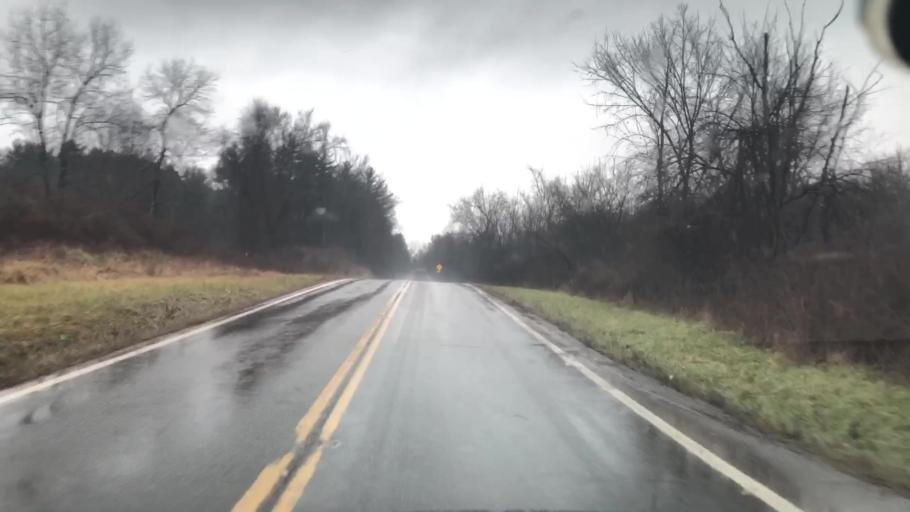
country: US
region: Ohio
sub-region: Harrison County
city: Cadiz
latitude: 40.1731
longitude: -80.9907
